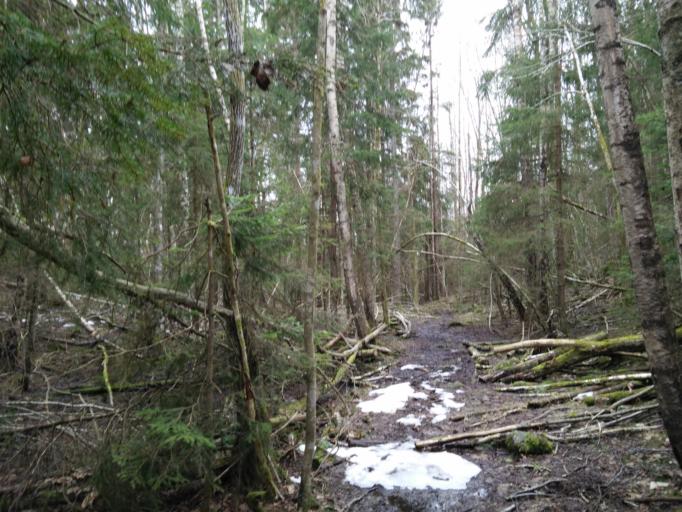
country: SE
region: OErebro
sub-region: Orebro Kommun
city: Garphyttan
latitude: 59.2838
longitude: 14.8952
